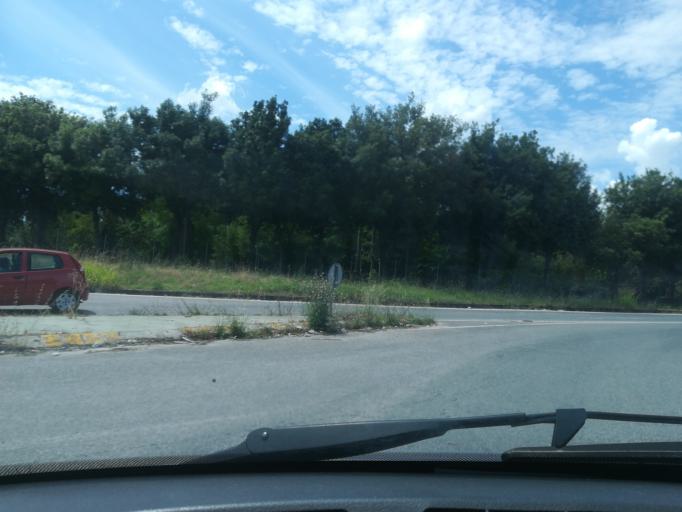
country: IT
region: The Marches
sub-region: Provincia di Macerata
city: Santa Maria Apparente
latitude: 43.2810
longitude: 13.6847
